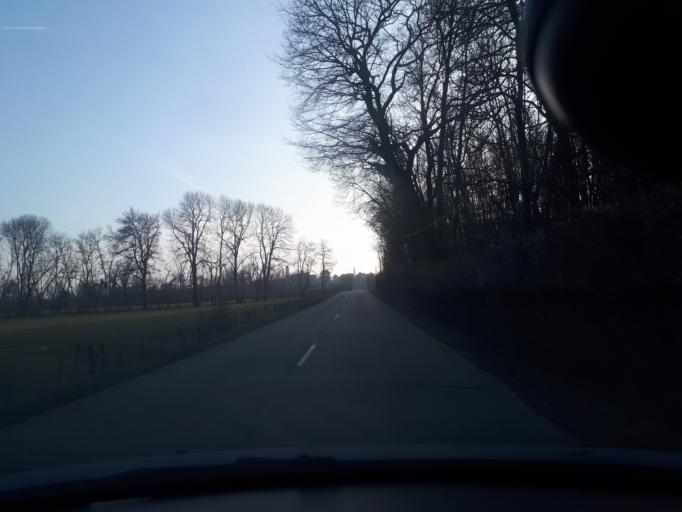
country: FR
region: Rhone-Alpes
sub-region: Departement de l'Isere
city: Creys-Mepieu
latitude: 45.7025
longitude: 5.5332
